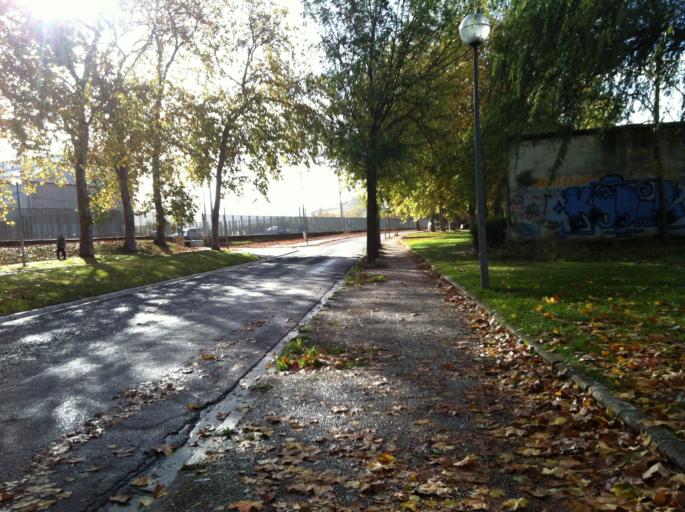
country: ES
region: Basque Country
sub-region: Provincia de Alava
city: Gasteiz / Vitoria
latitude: 42.8345
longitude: -2.6658
